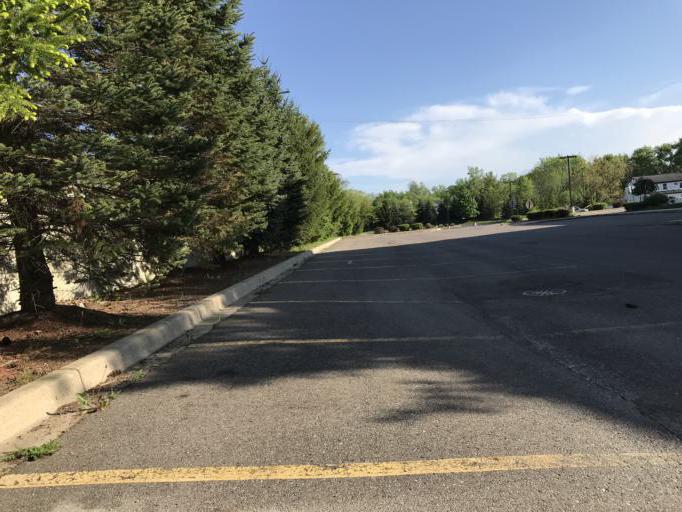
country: US
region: Michigan
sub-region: Oakland County
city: Farmington
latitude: 42.4701
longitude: -83.3402
